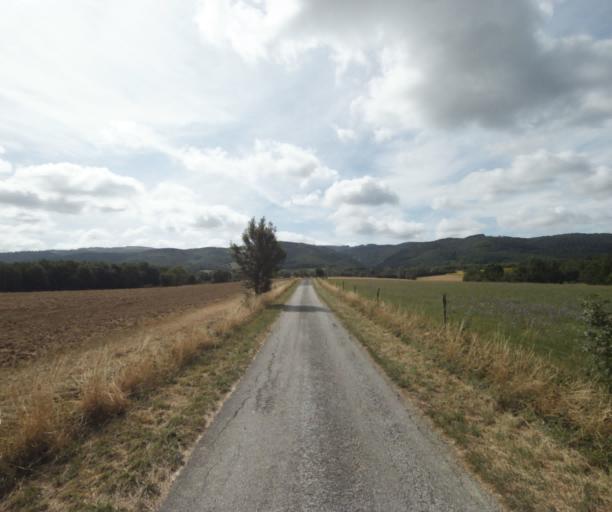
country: FR
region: Midi-Pyrenees
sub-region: Departement du Tarn
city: Soreze
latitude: 43.4763
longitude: 2.0971
